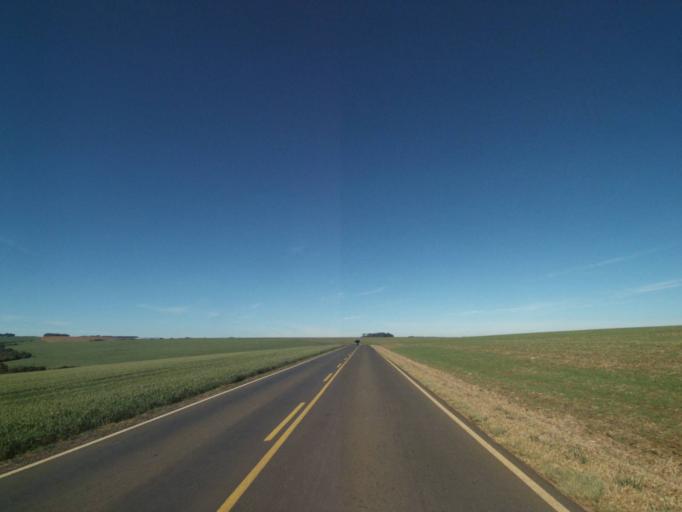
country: BR
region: Parana
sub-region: Tibagi
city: Tibagi
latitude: -24.5587
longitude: -50.2905
